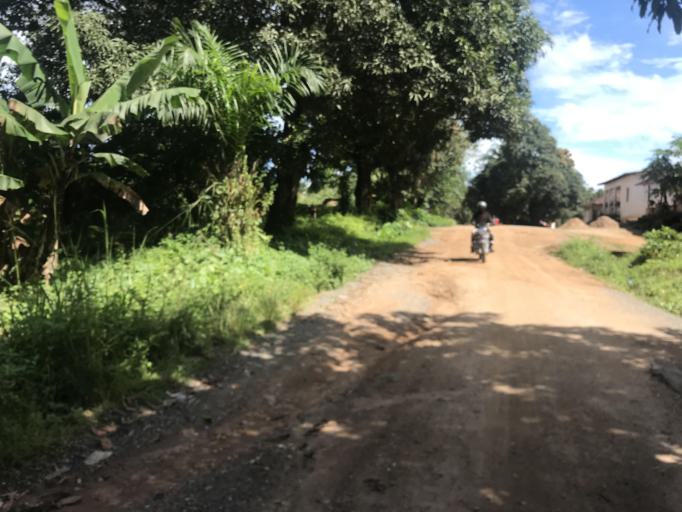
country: SL
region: Eastern Province
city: Koidu
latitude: 8.6414
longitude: -10.9879
